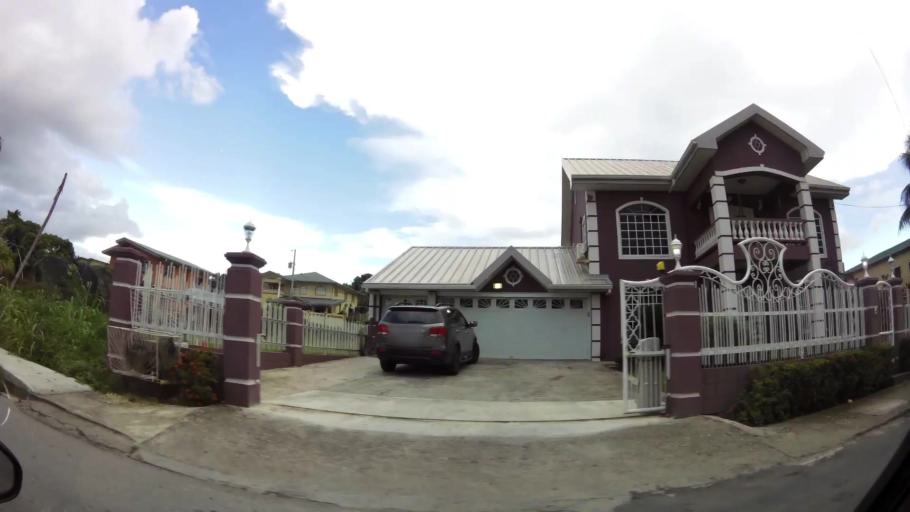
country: TT
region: City of San Fernando
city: Mon Repos
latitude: 10.2577
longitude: -61.4583
